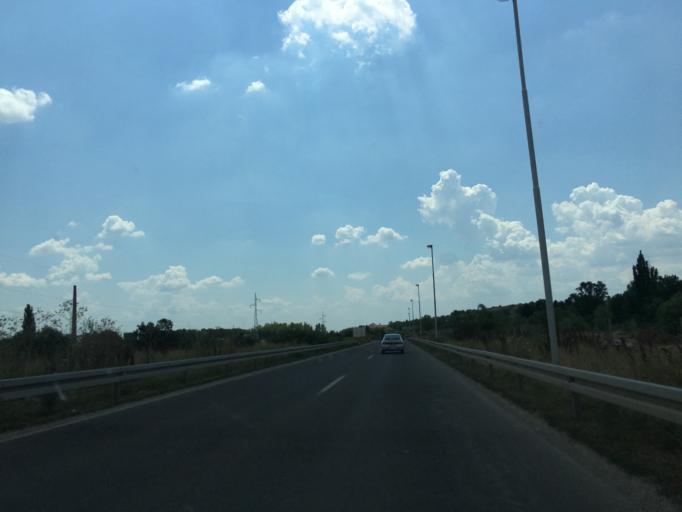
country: RS
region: Central Serbia
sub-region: Belgrade
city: Mladenovac
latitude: 44.4367
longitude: 20.6844
